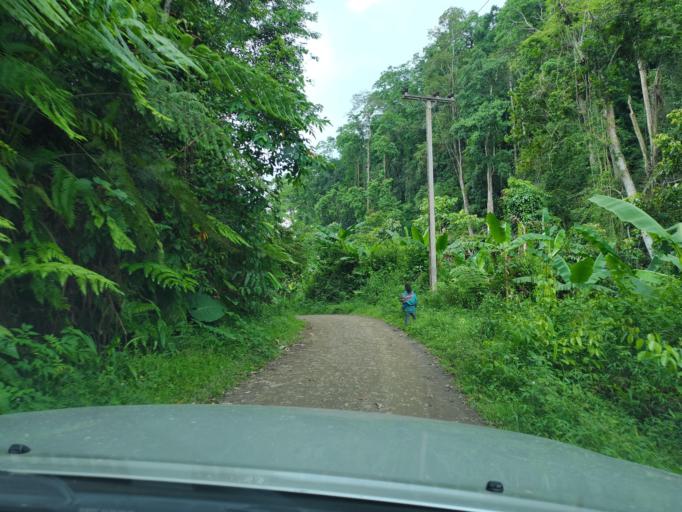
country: LA
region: Loungnamtha
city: Muang Long
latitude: 20.7770
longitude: 101.0168
